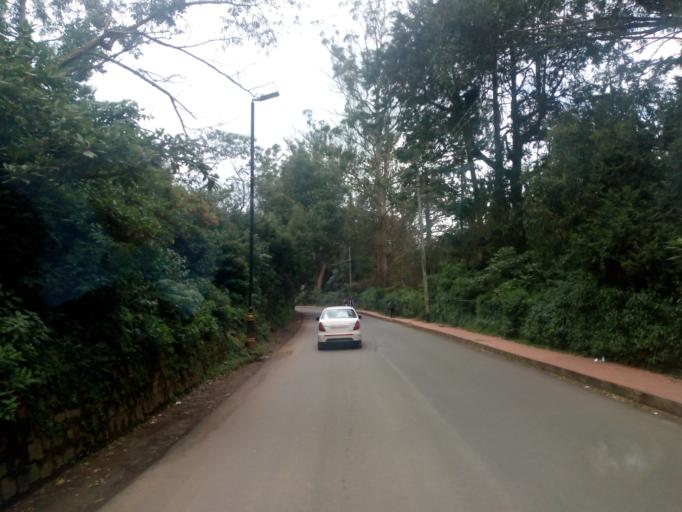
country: IN
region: Tamil Nadu
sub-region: Nilgiri
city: Ooty
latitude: 11.4058
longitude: 76.6901
